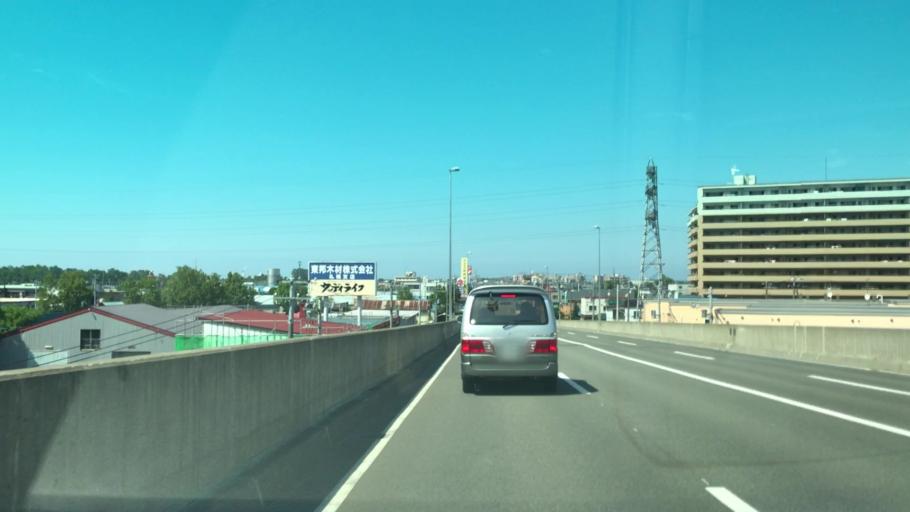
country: JP
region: Hokkaido
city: Sapporo
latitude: 43.1253
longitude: 141.2359
